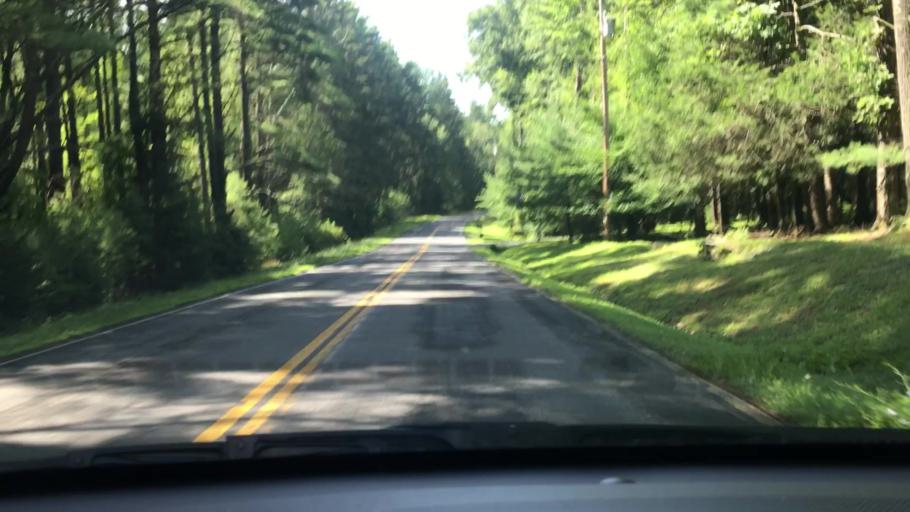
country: US
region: New York
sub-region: Ulster County
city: Shokan
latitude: 41.9381
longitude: -74.2433
